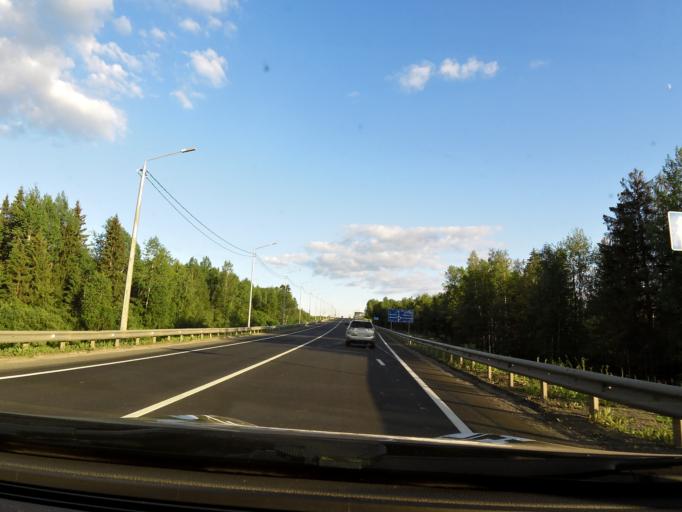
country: RU
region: Vologda
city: Gryazovets
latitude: 59.0264
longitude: 40.1131
